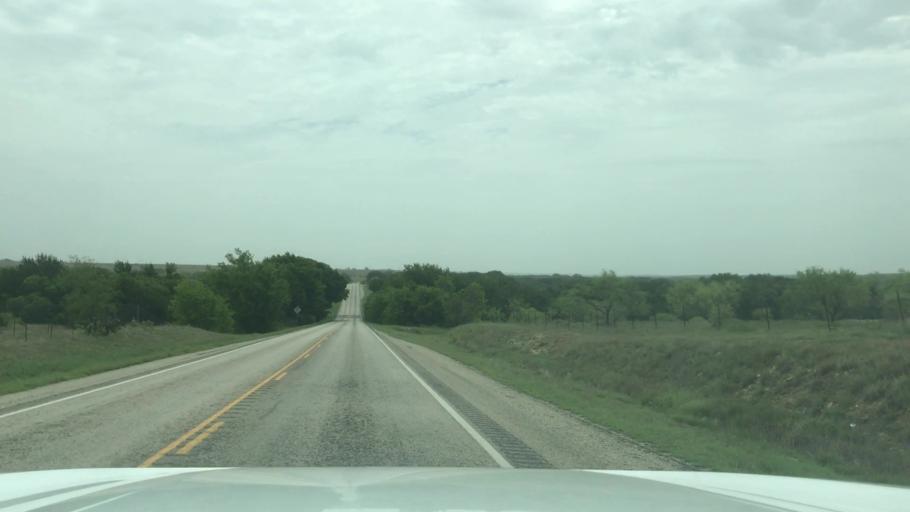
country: US
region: Texas
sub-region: Erath County
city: Dublin
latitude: 32.0578
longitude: -98.1990
